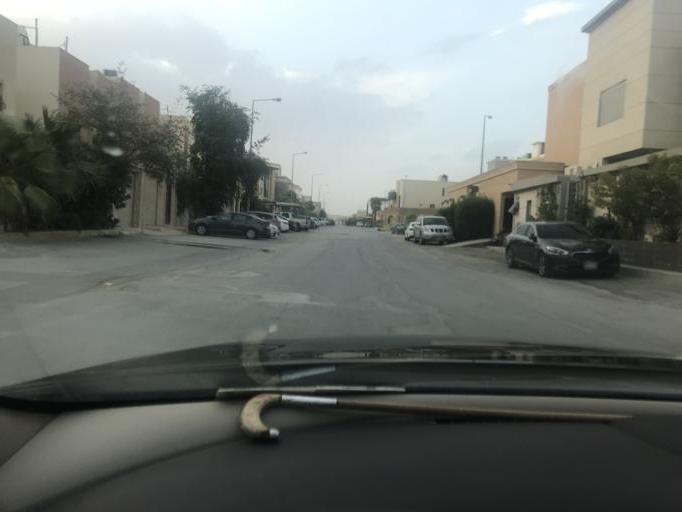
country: SA
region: Ar Riyad
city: Riyadh
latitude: 24.7279
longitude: 46.7455
